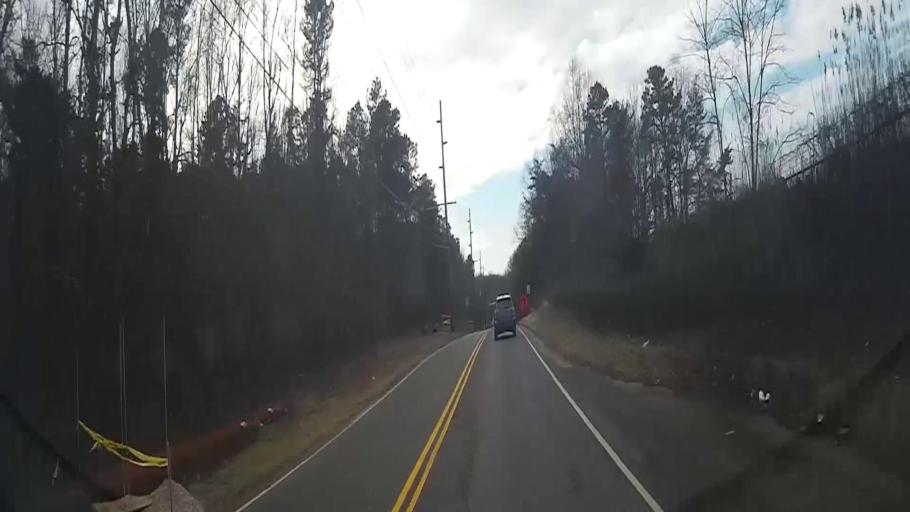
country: US
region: New Jersey
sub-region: Camden County
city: Pine Hill
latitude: 39.7780
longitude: -75.0213
